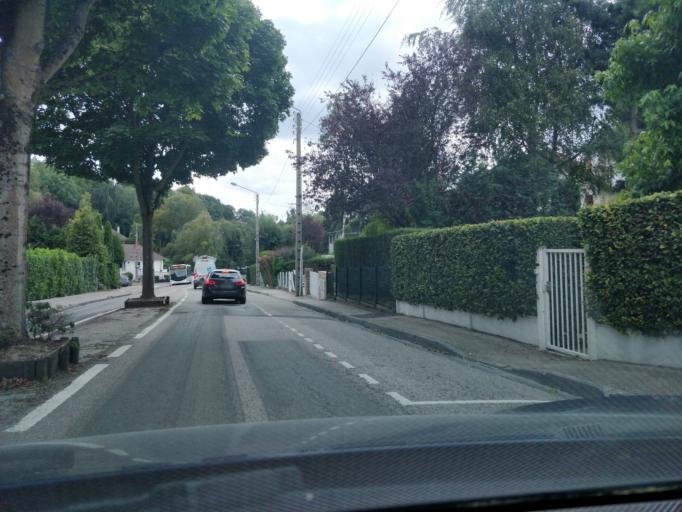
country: FR
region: Haute-Normandie
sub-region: Departement de la Seine-Maritime
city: Mont-Saint-Aignan
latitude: 49.4696
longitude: 1.1083
